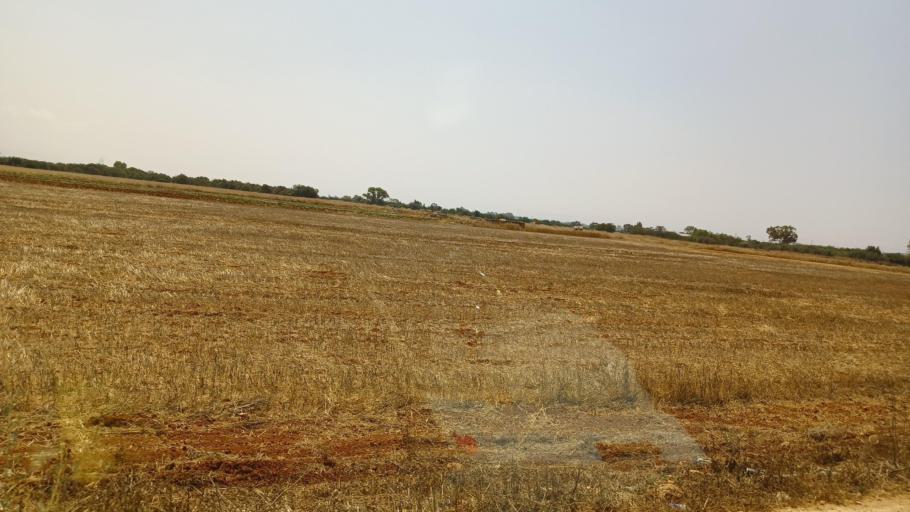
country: CY
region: Ammochostos
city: Liopetri
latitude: 34.9799
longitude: 33.8665
